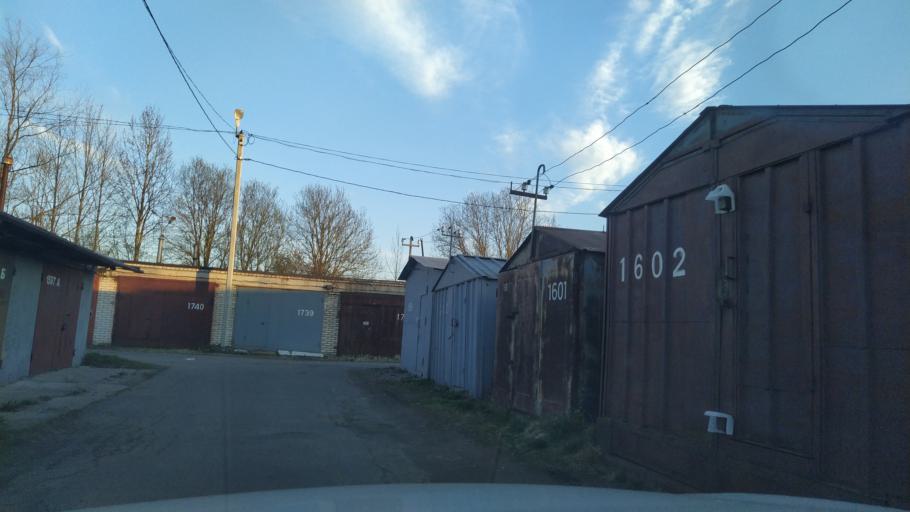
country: RU
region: St.-Petersburg
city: Pushkin
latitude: 59.6914
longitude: 30.3943
